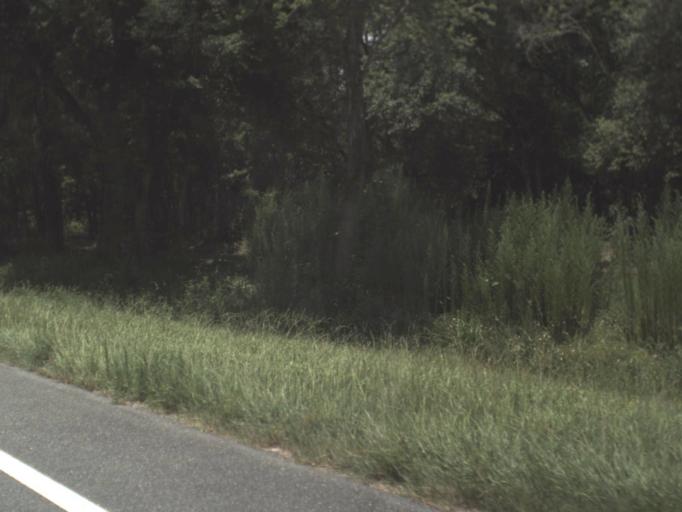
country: US
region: Florida
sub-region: Columbia County
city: Five Points
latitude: 30.2872
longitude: -82.7035
